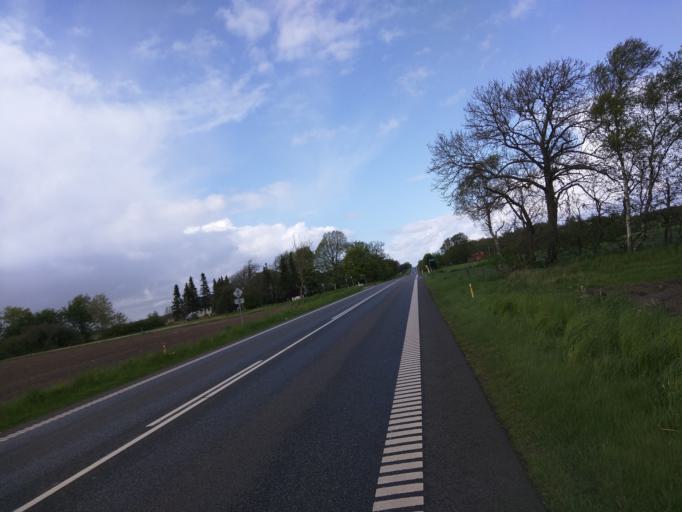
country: DK
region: Central Jutland
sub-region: Viborg Kommune
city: Viborg
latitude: 56.3760
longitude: 9.4414
